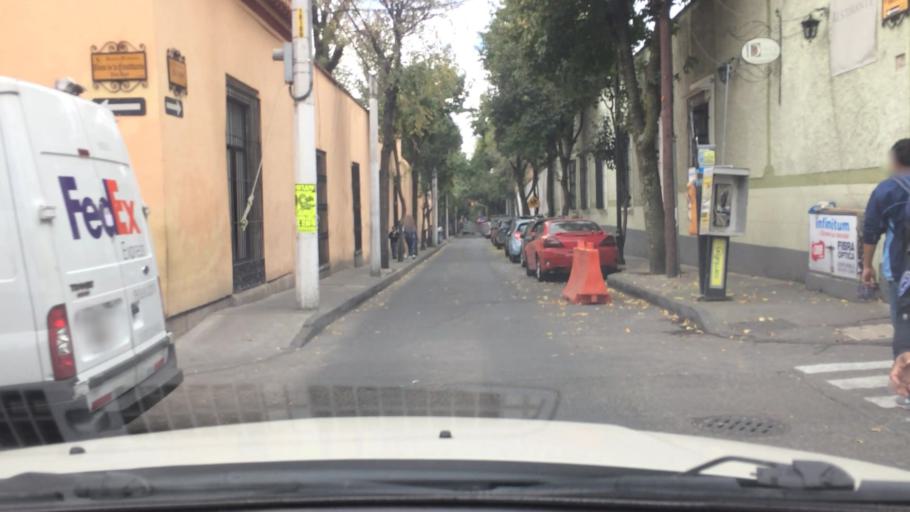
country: MX
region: Mexico City
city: Tlalpan
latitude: 19.2878
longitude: -99.1670
